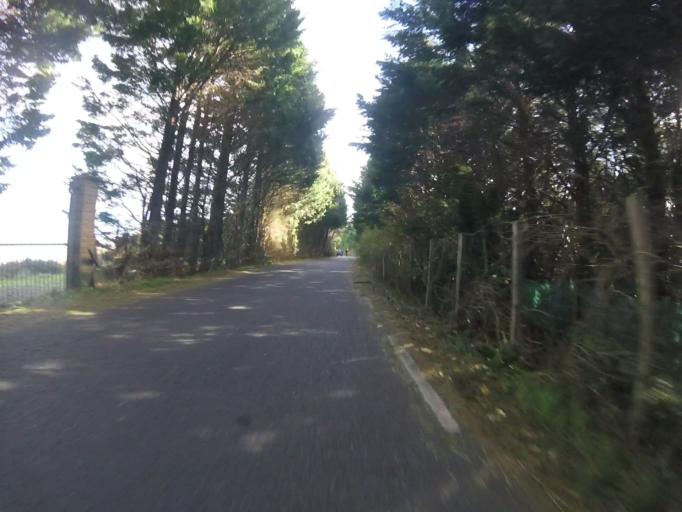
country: ES
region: Basque Country
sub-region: Provincia de Guipuzcoa
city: Usurbil
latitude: 43.2950
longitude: -2.0831
